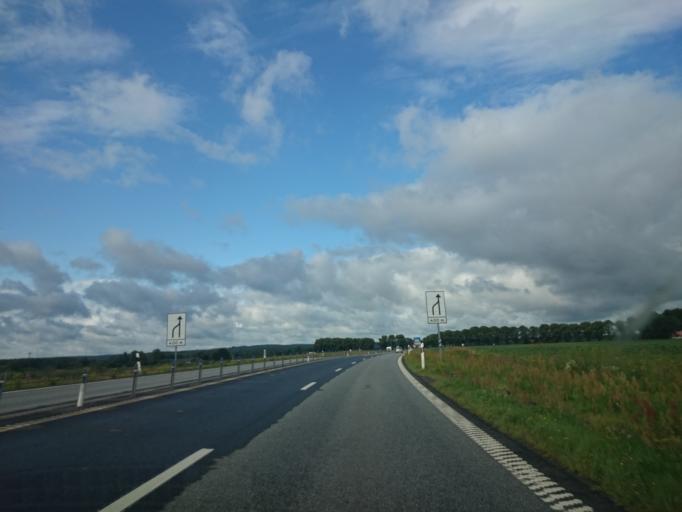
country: SE
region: Skane
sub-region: Kristianstads Kommun
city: Degeberga
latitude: 55.9360
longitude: 14.0363
